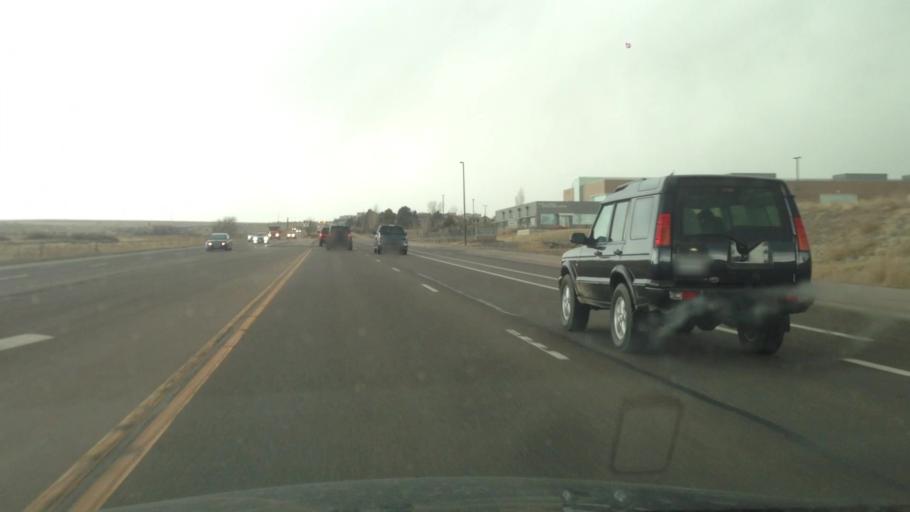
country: US
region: Colorado
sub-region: Douglas County
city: Parker
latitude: 39.4931
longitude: -104.7853
